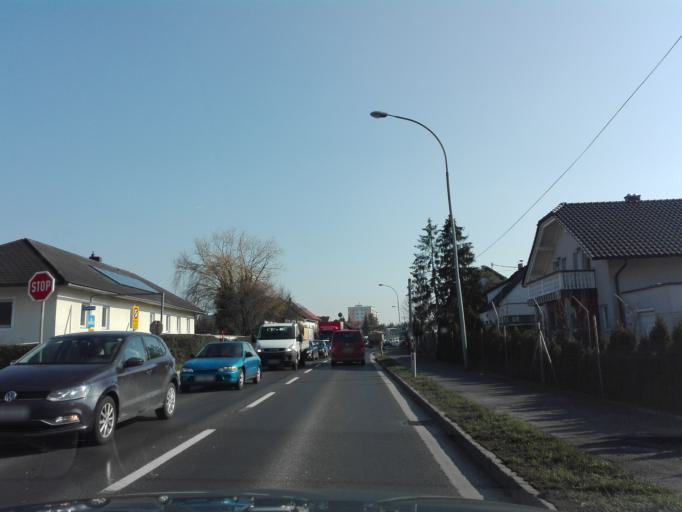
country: AT
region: Upper Austria
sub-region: Politischer Bezirk Linz-Land
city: Traun
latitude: 48.2081
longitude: 14.2457
